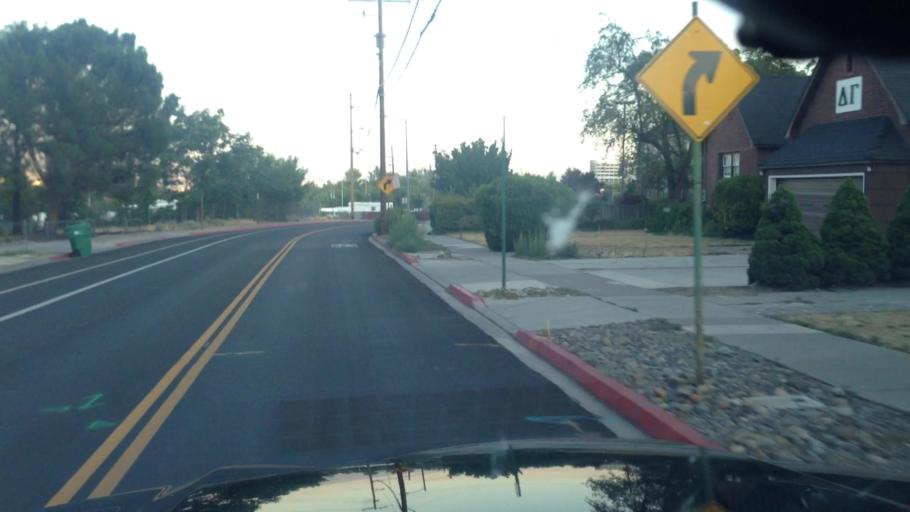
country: US
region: Nevada
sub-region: Washoe County
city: Reno
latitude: 39.5392
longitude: -119.8113
